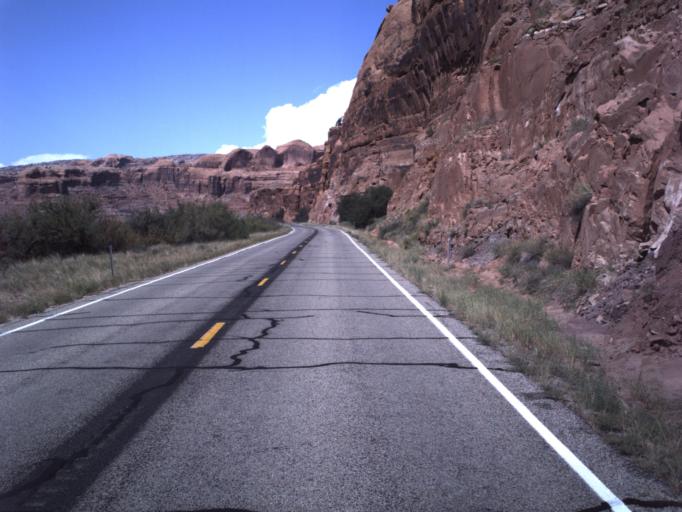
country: US
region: Utah
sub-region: Grand County
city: Moab
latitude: 38.5598
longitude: -109.6314
